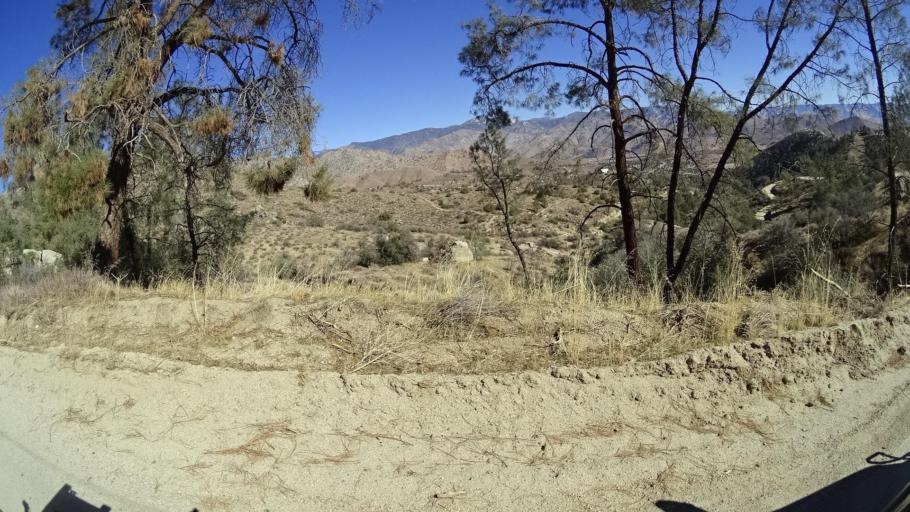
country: US
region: California
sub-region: Kern County
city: Wofford Heights
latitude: 35.7001
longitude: -118.4866
